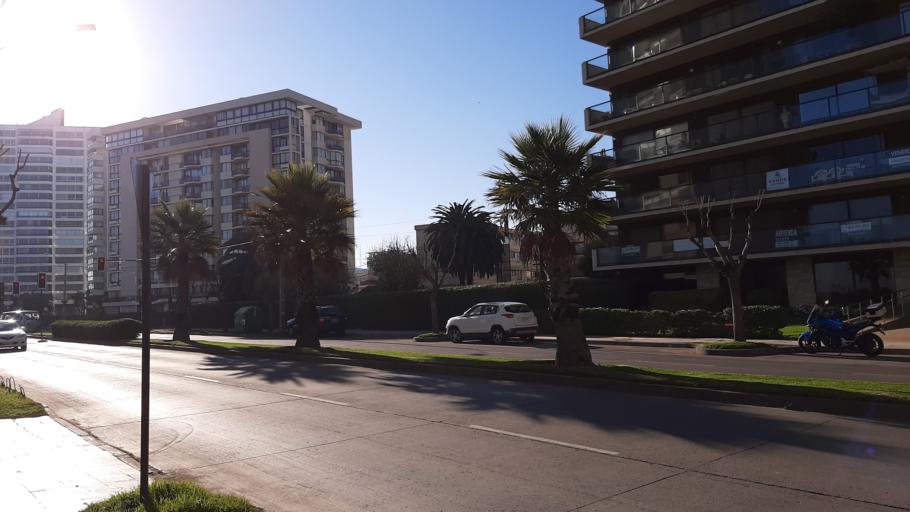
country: CL
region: Valparaiso
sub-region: Provincia de Valparaiso
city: Vina del Mar
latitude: -33.0132
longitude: -71.5542
